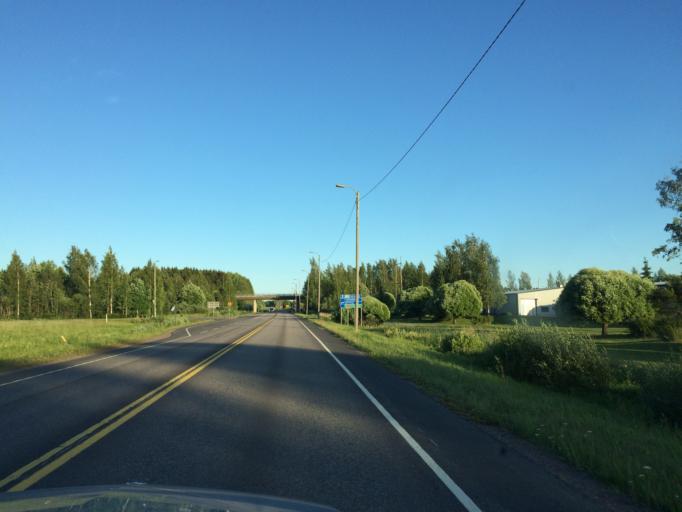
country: FI
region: Haeme
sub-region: Haemeenlinna
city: Tervakoski
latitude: 60.8201
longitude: 24.6382
